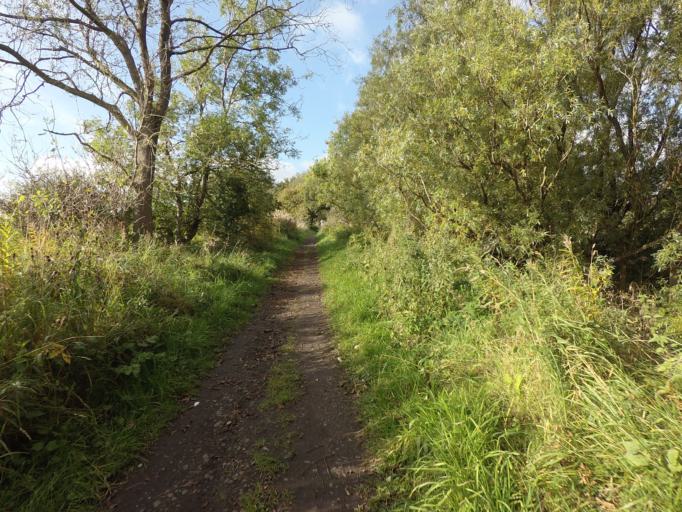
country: GB
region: Scotland
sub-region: West Lothian
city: East Calder
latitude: 55.9048
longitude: -3.4700
